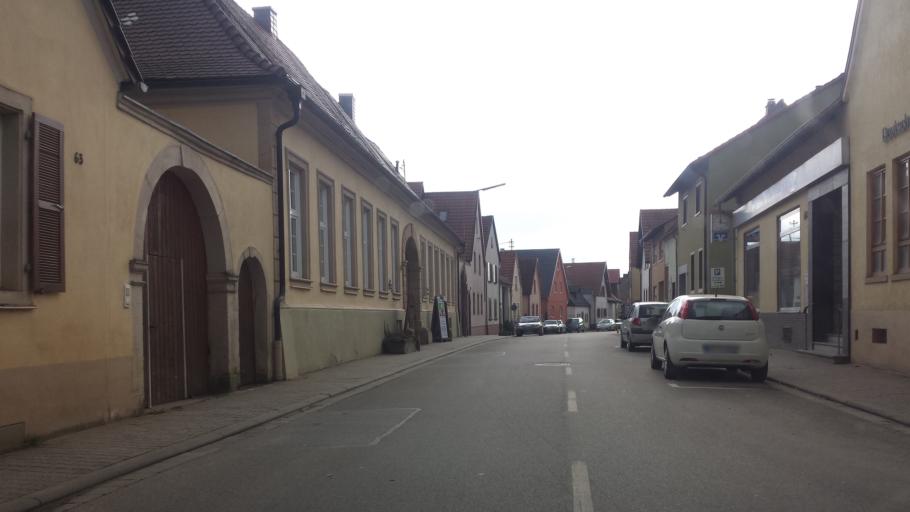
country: DE
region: Rheinland-Pfalz
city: Fussgonheim
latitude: 49.4578
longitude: 8.2940
